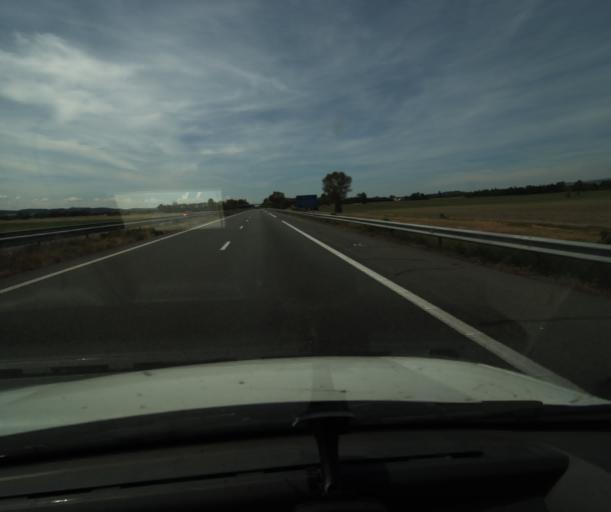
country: FR
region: Languedoc-Roussillon
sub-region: Departement de l'Aude
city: Saint-Martin-Lalande
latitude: 43.2640
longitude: 2.0175
